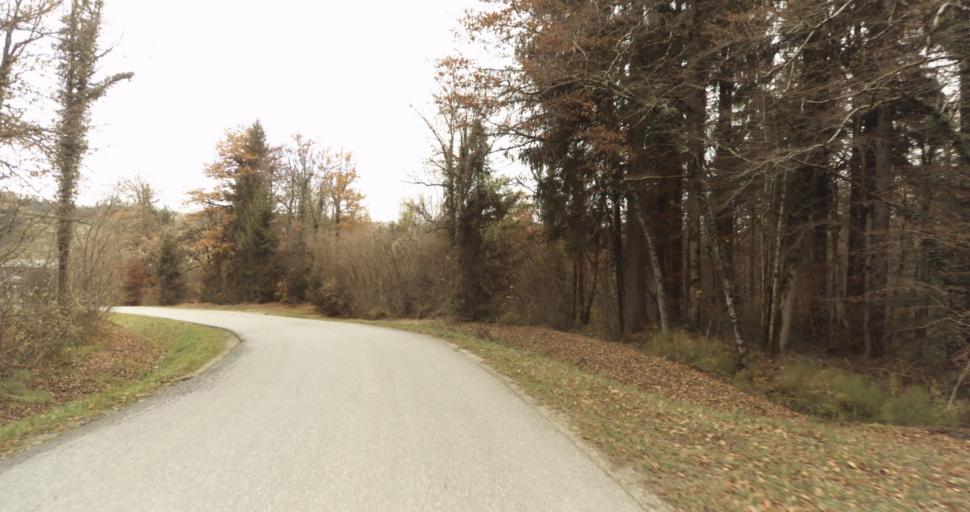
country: FR
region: Rhone-Alpes
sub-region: Departement de la Haute-Savoie
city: Groisy
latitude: 45.9976
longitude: 6.1827
